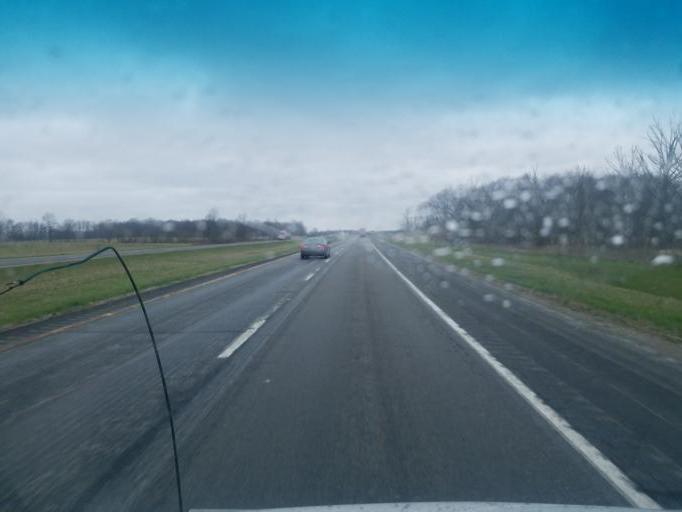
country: US
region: Ohio
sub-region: Hardin County
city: Forest
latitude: 40.8249
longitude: -83.5536
